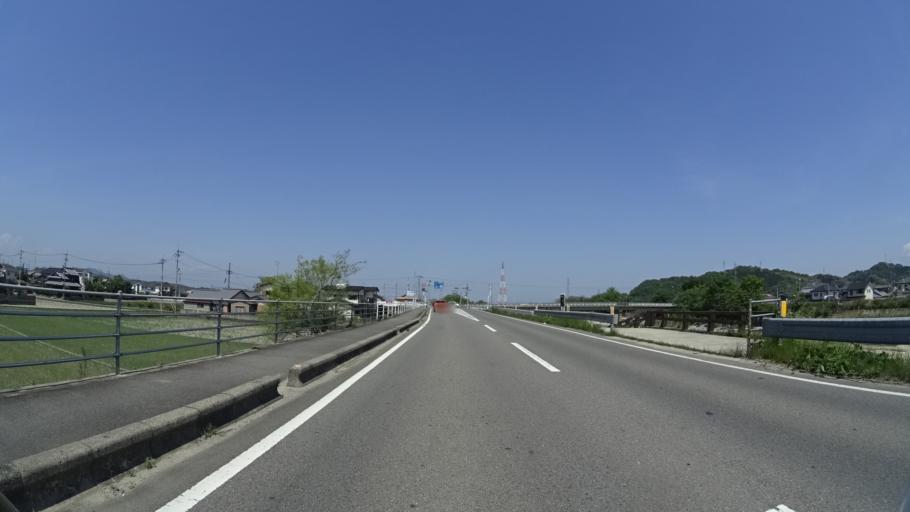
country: JP
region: Ehime
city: Hojo
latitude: 34.0317
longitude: 132.9675
